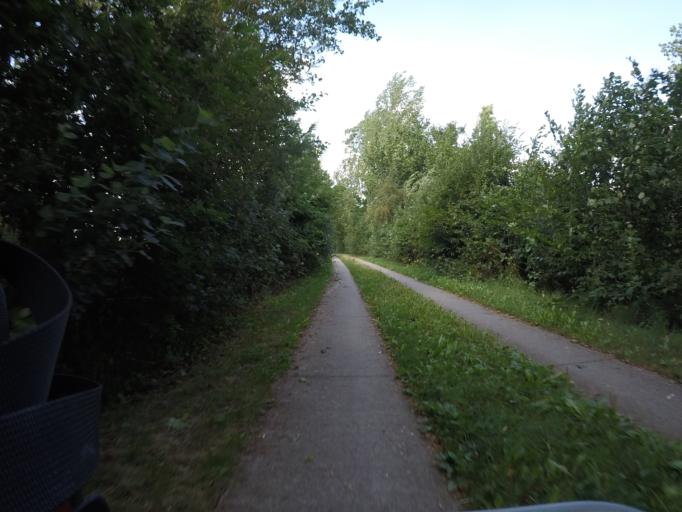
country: DE
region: Lower Saxony
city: Stelle
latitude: 53.4402
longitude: 10.1360
